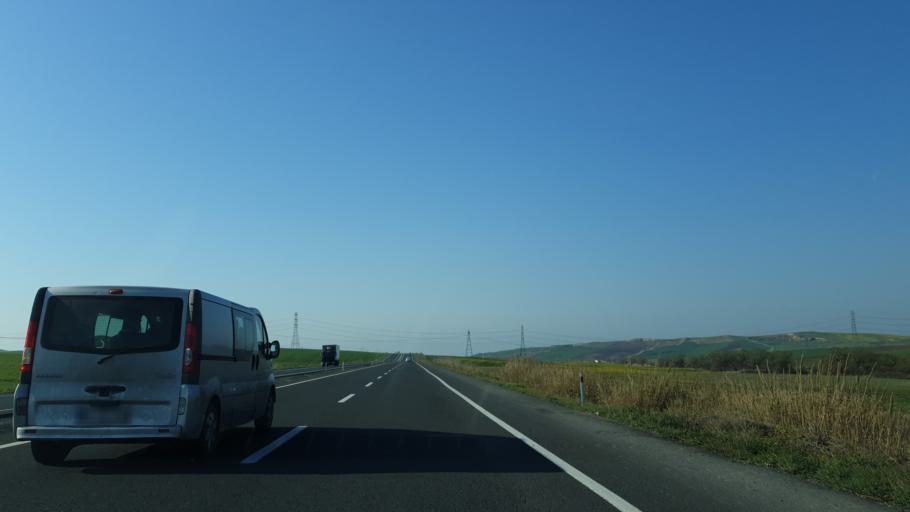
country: TR
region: Tekirdag
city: Corlu
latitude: 41.0810
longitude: 27.7420
